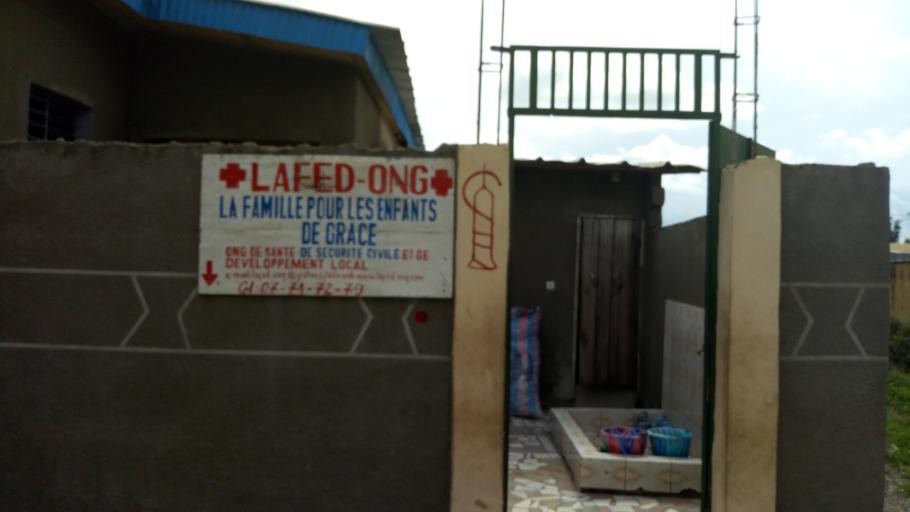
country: CI
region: Vallee du Bandama
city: Bouake
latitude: 7.7280
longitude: -5.0247
